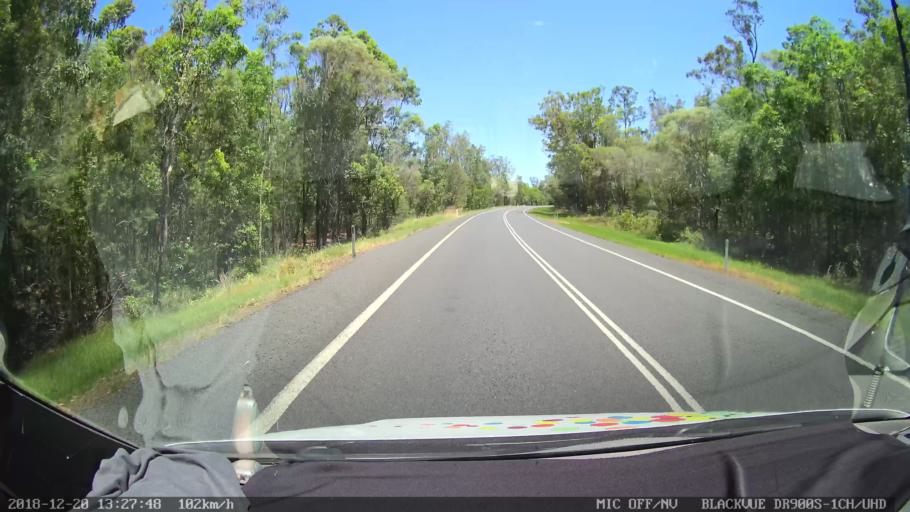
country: AU
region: New South Wales
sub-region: Clarence Valley
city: Gordon
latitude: -29.1655
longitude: 152.9931
